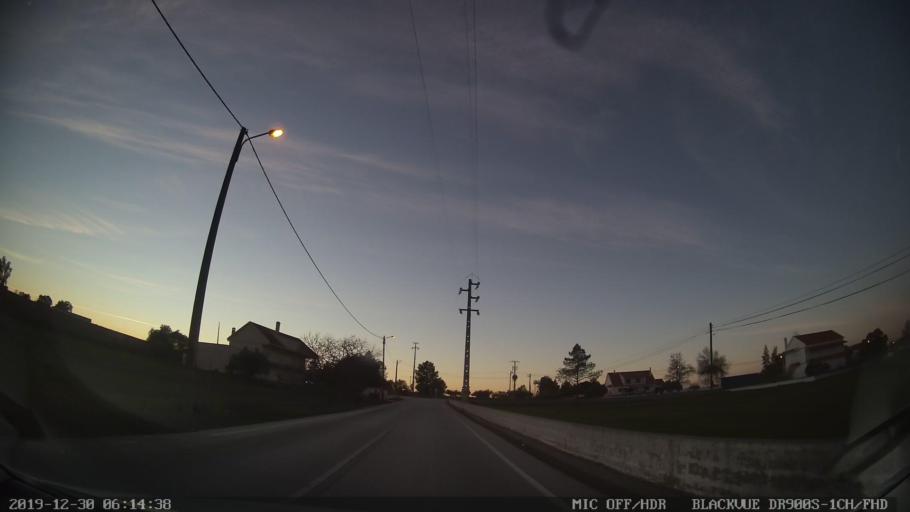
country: PT
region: Castelo Branco
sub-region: Penamacor
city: Penamacor
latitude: 40.1129
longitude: -7.2195
